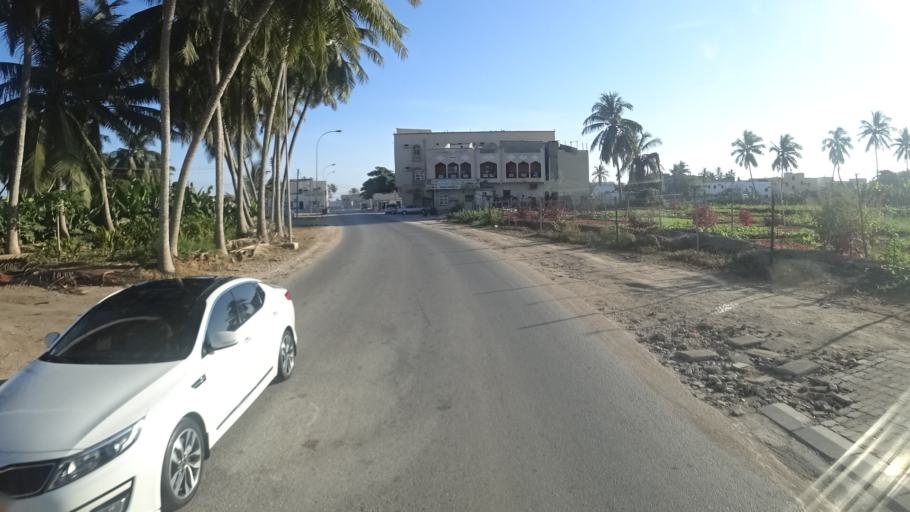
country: OM
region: Zufar
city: Salalah
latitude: 17.0044
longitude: 54.1044
